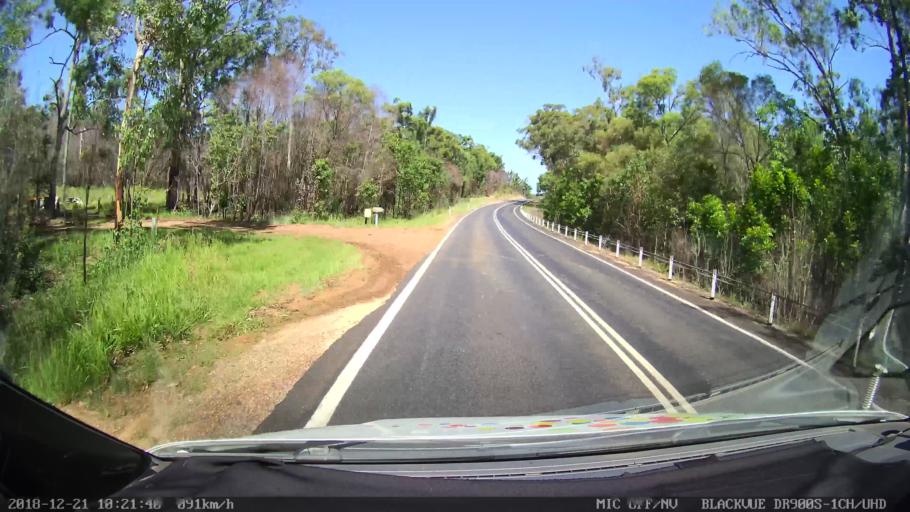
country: AU
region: New South Wales
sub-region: Clarence Valley
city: South Grafton
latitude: -29.6599
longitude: 152.8104
